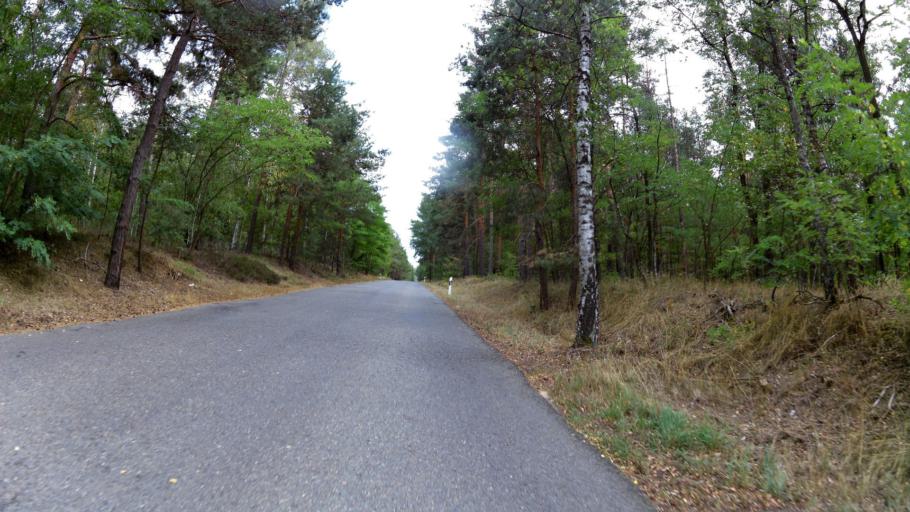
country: DE
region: Brandenburg
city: Spremberg
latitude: 51.6488
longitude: 14.3777
